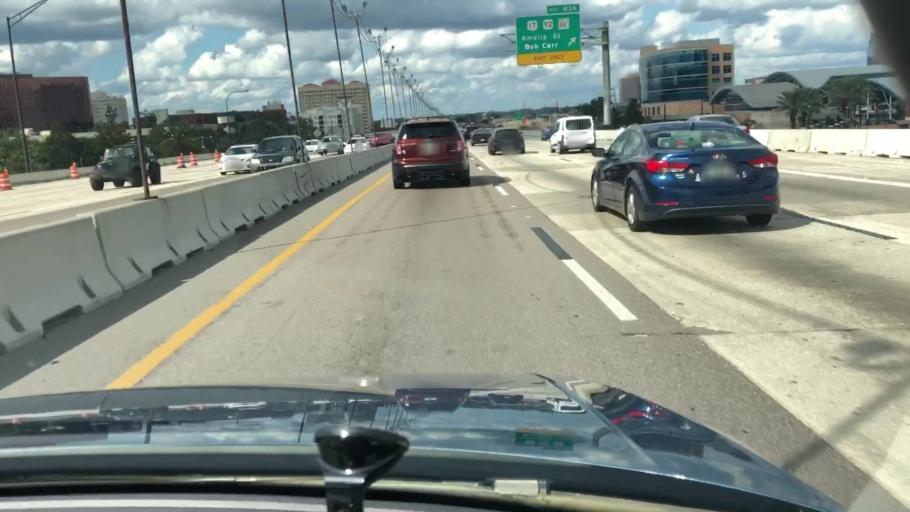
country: US
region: Florida
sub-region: Orange County
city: Orlando
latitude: 28.5464
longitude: -81.3824
